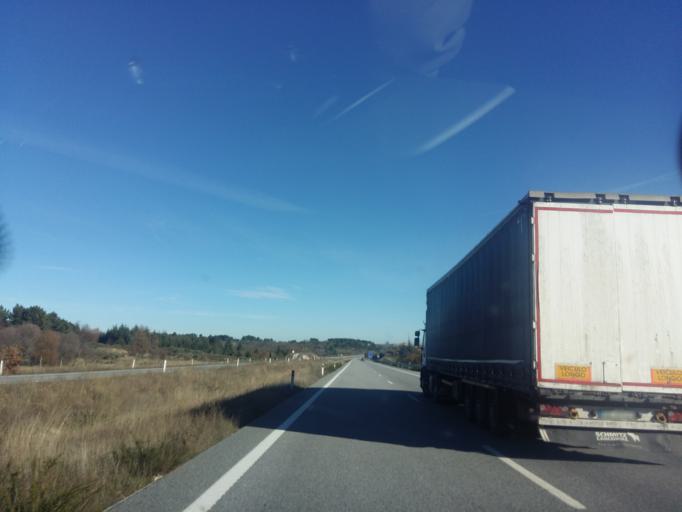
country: PT
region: Guarda
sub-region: Guarda
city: Sequeira
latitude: 40.6020
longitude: -7.0877
